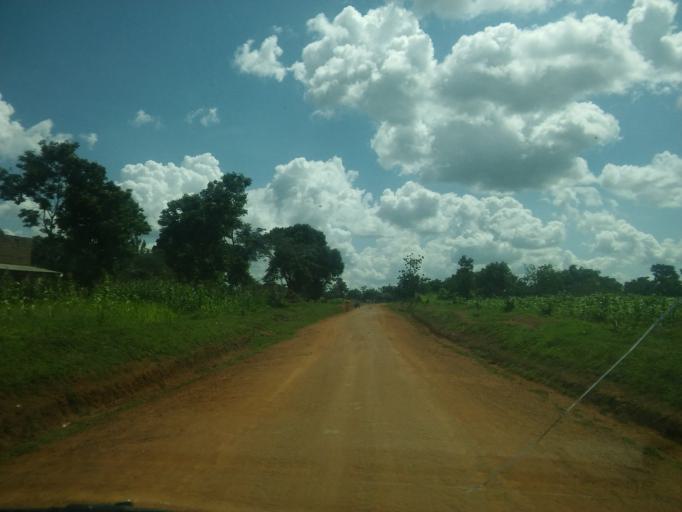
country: UG
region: Eastern Region
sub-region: Pallisa District
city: Pallisa
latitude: 1.1513
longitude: 33.8095
